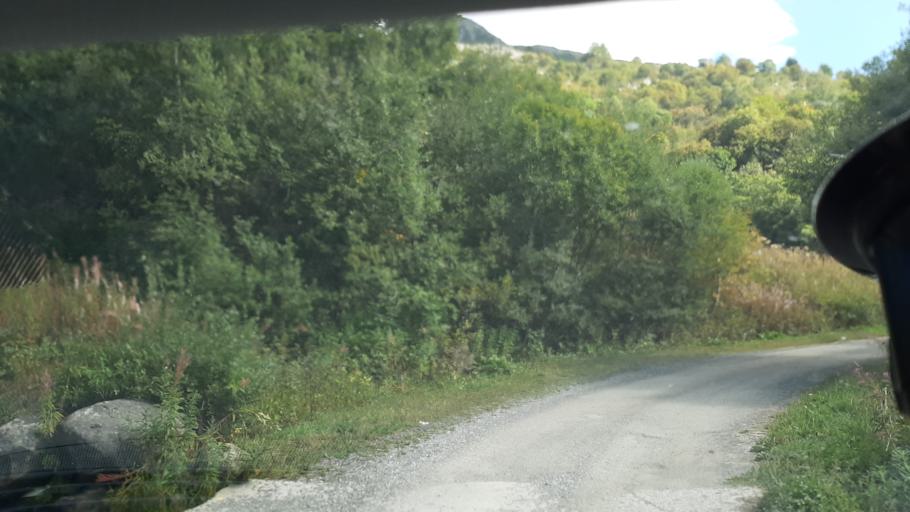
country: FR
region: Rhone-Alpes
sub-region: Departement de la Savoie
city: Saint-Michel-de-Maurienne
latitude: 45.1686
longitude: 6.4947
